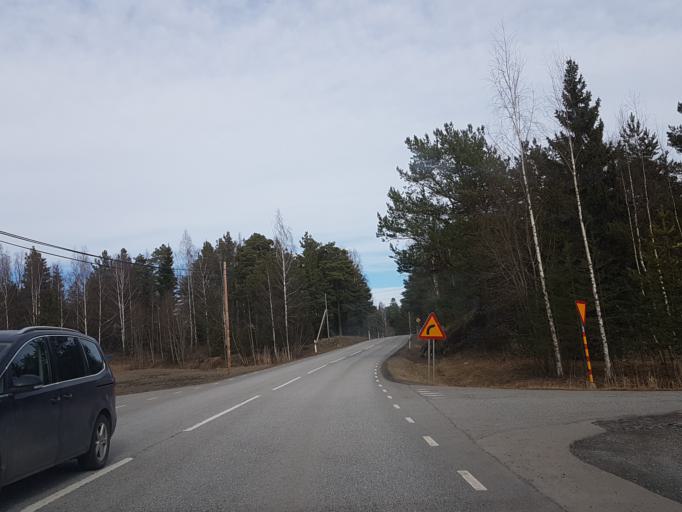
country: SE
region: Stockholm
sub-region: Norrtalje Kommun
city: Norrtalje
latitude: 59.6815
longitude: 18.8155
